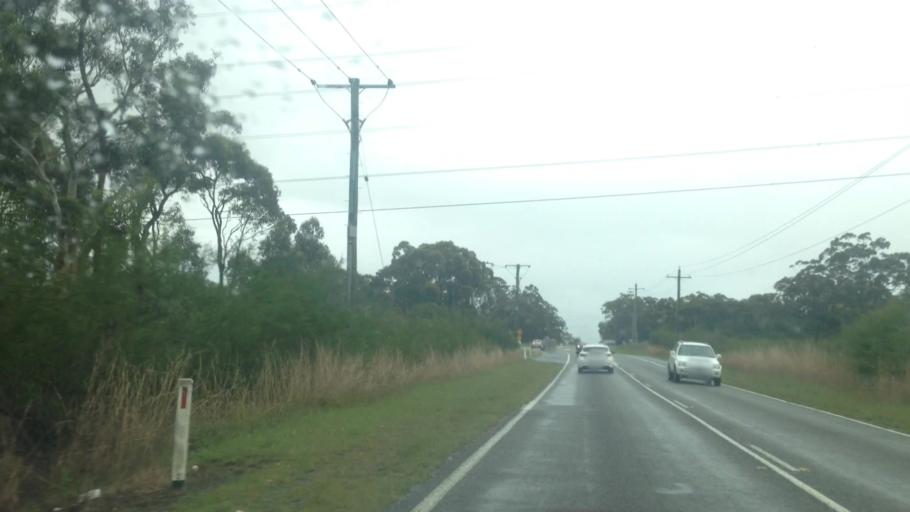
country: AU
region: New South Wales
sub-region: Wyong Shire
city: Charmhaven
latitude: -33.1585
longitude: 151.4786
